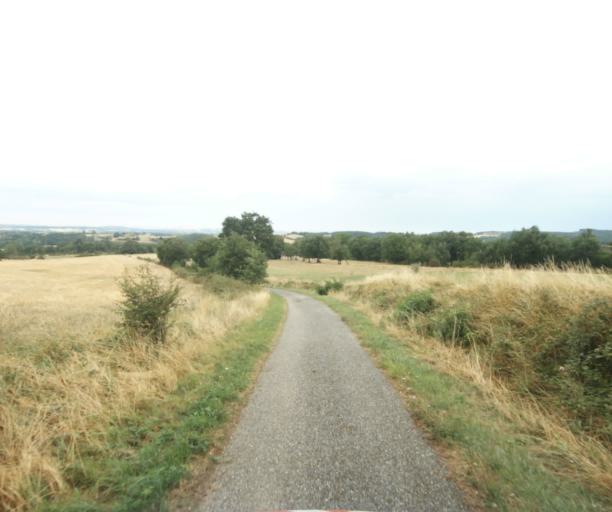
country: FR
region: Midi-Pyrenees
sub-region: Departement de la Haute-Garonne
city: Revel
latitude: 43.4151
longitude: 1.9816
